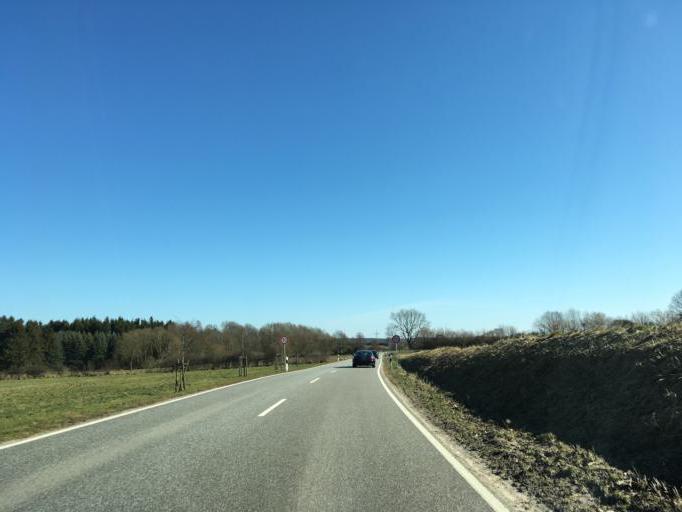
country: DE
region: Schleswig-Holstein
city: Sierksrade
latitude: 53.7361
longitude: 10.6038
